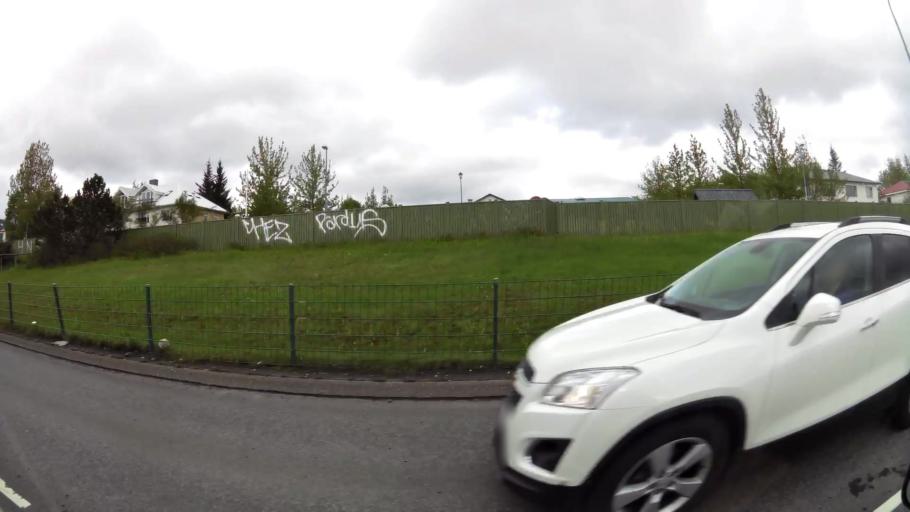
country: IS
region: Capital Region
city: Reykjavik
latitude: 64.1223
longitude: -21.8745
